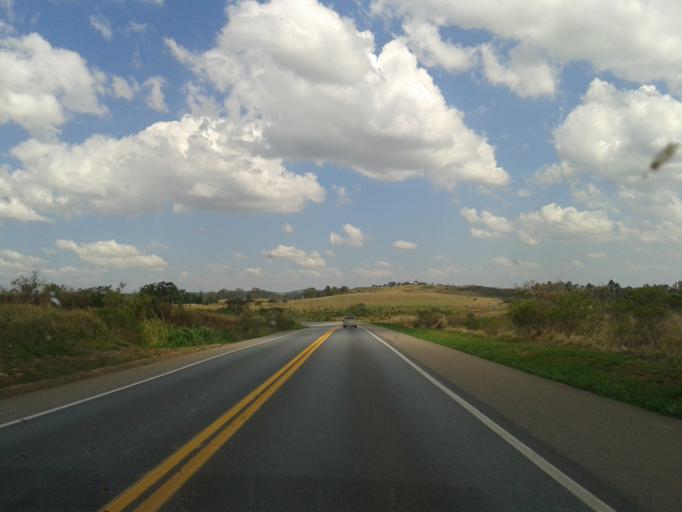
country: BR
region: Minas Gerais
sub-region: Campos Altos
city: Campos Altos
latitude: -19.6892
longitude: -46.0384
